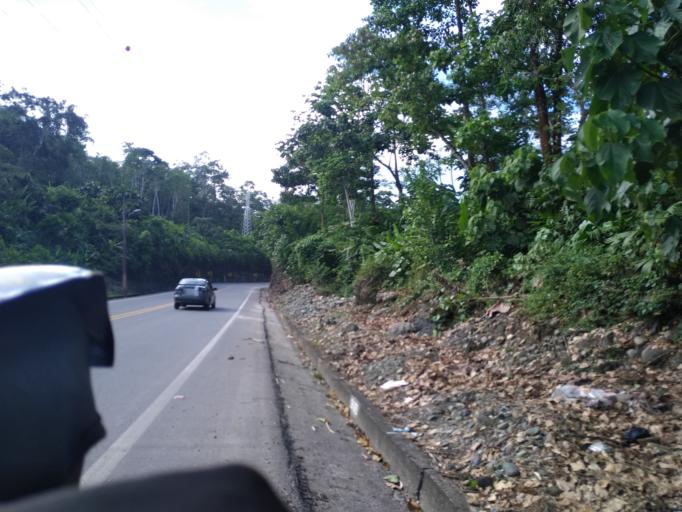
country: EC
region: Napo
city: Tena
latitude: -1.0423
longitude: -77.7970
